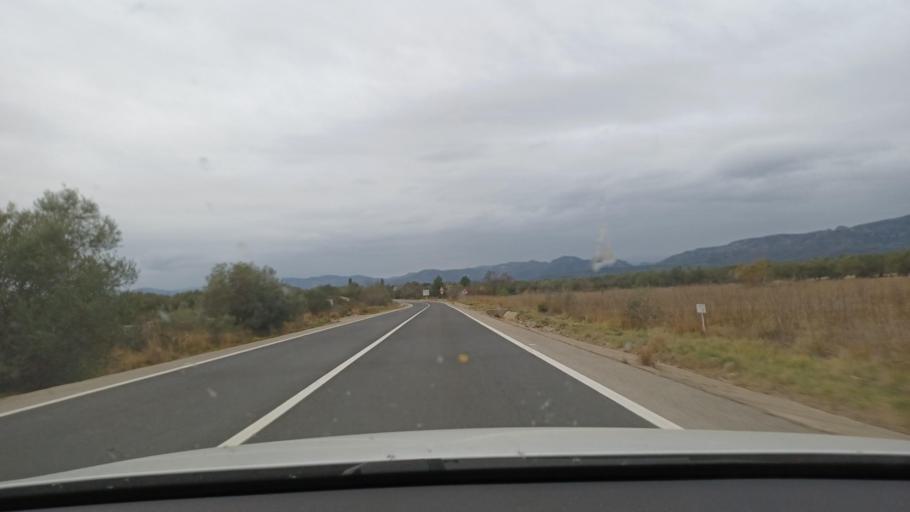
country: ES
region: Catalonia
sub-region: Provincia de Tarragona
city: Mas de Barberans
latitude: 40.6413
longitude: 0.3583
